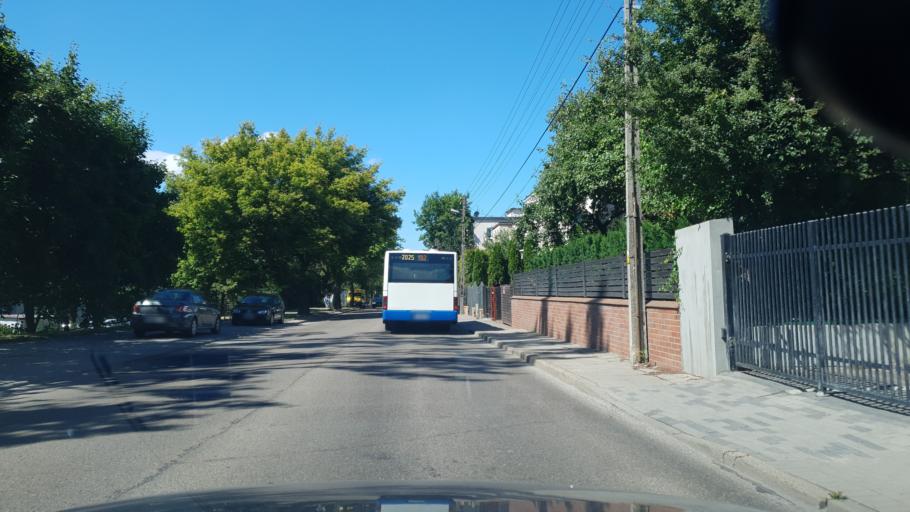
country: PL
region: Pomeranian Voivodeship
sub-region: Gdynia
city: Gdynia
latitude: 54.4998
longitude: 18.5417
